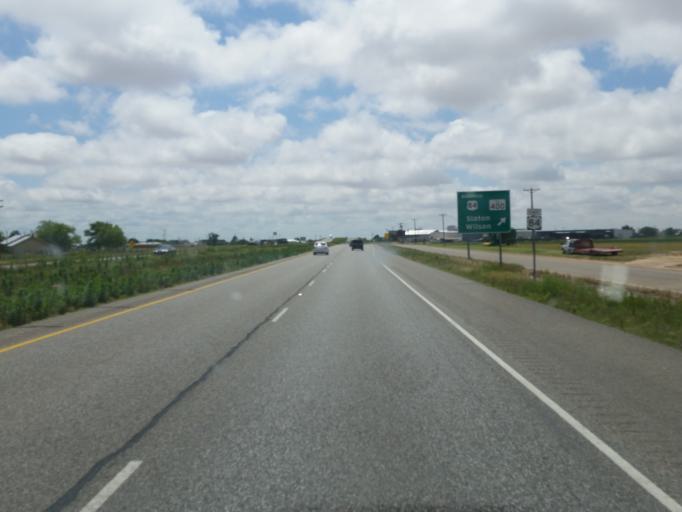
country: US
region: Texas
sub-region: Lubbock County
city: Slaton
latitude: 33.4243
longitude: -101.6505
